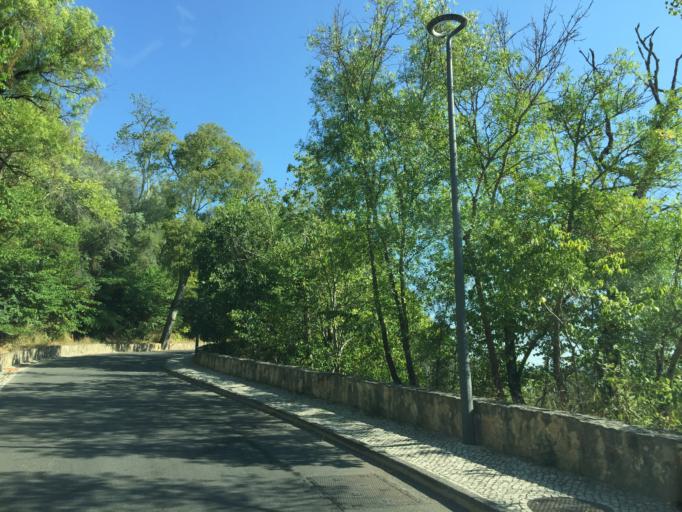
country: PT
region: Santarem
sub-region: Tomar
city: Tomar
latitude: 39.6033
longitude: -8.4160
